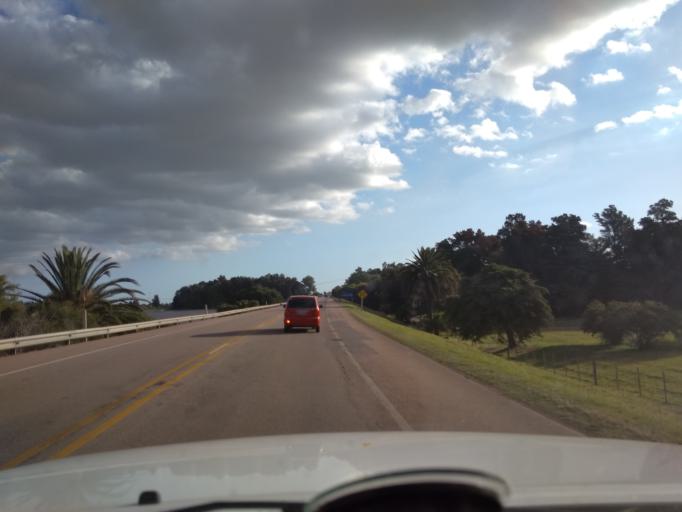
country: UY
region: Canelones
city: Canelones
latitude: -34.4574
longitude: -56.2678
